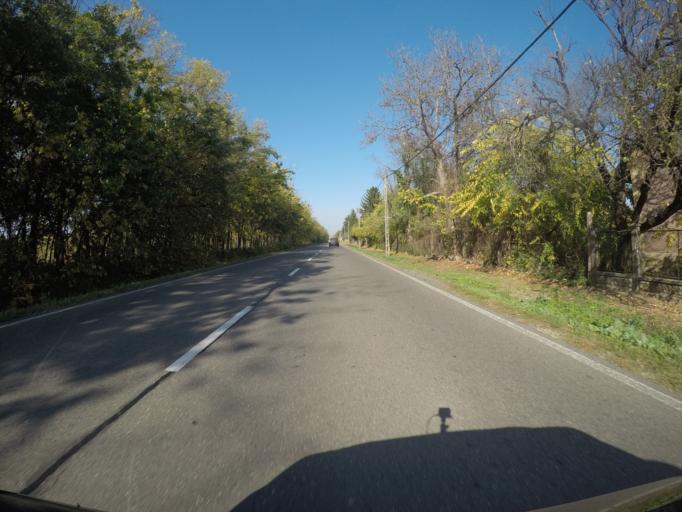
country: HU
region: Tolna
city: Szedres
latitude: 46.5145
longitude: 18.6639
